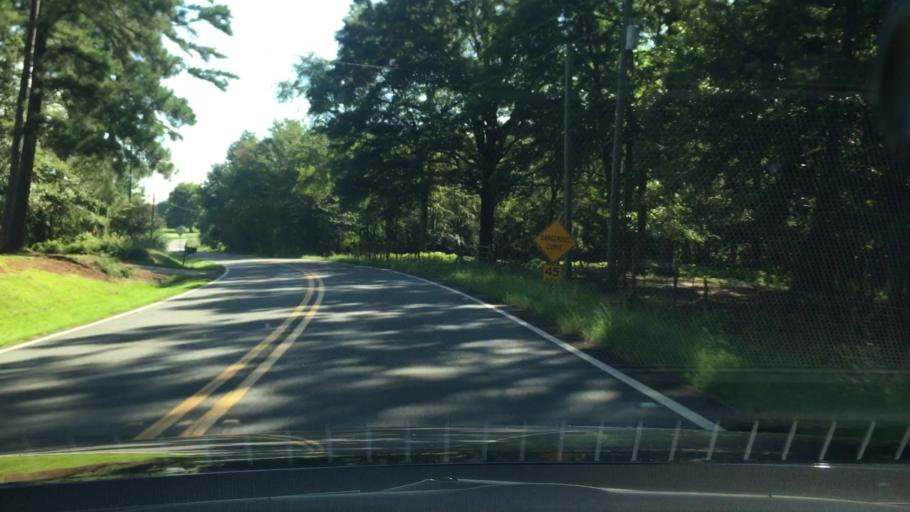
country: US
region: Georgia
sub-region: Putnam County
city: Jefferson
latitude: 33.4403
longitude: -83.3483
